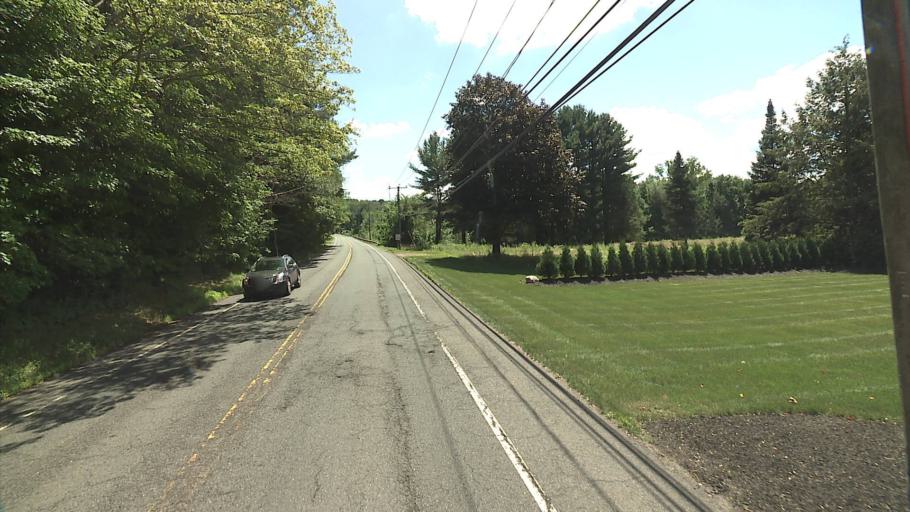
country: US
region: Massachusetts
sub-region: Hampden County
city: Southwick
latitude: 42.0186
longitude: -72.7272
